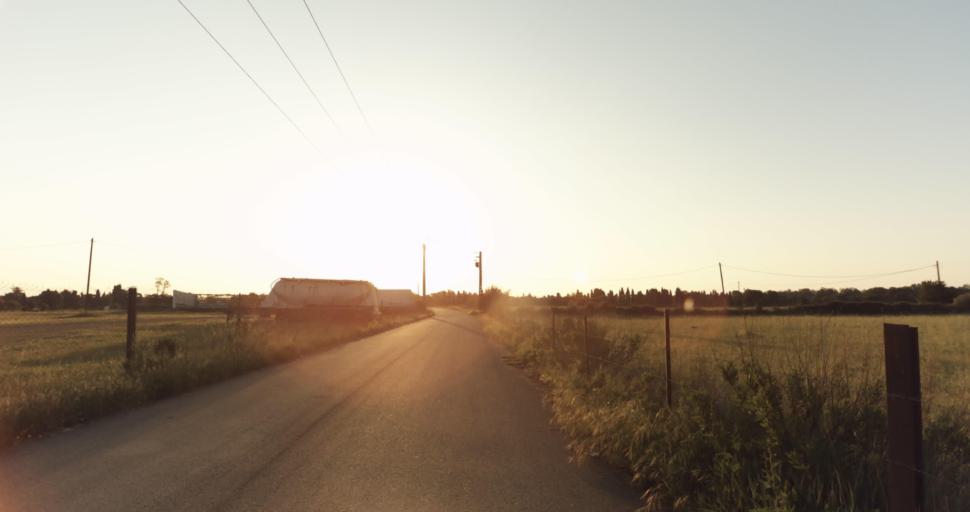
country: FR
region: Corsica
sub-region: Departement de la Haute-Corse
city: Biguglia
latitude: 42.5993
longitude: 9.4510
